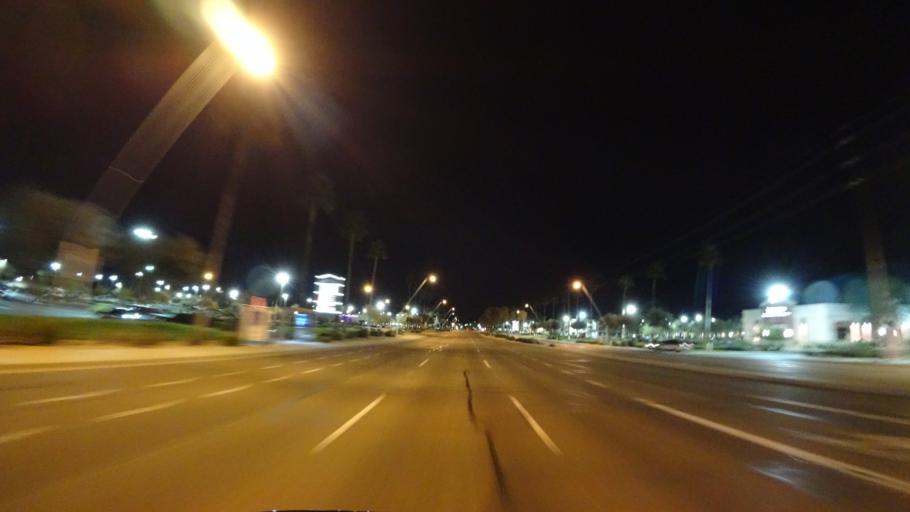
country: US
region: Arizona
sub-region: Maricopa County
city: Guadalupe
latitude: 33.3200
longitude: -111.9678
